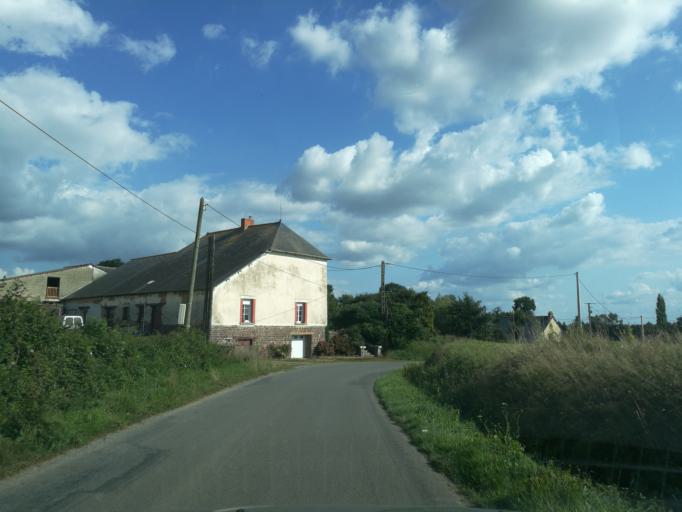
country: FR
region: Brittany
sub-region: Departement d'Ille-et-Vilaine
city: Bedee
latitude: 48.1899
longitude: -1.9557
